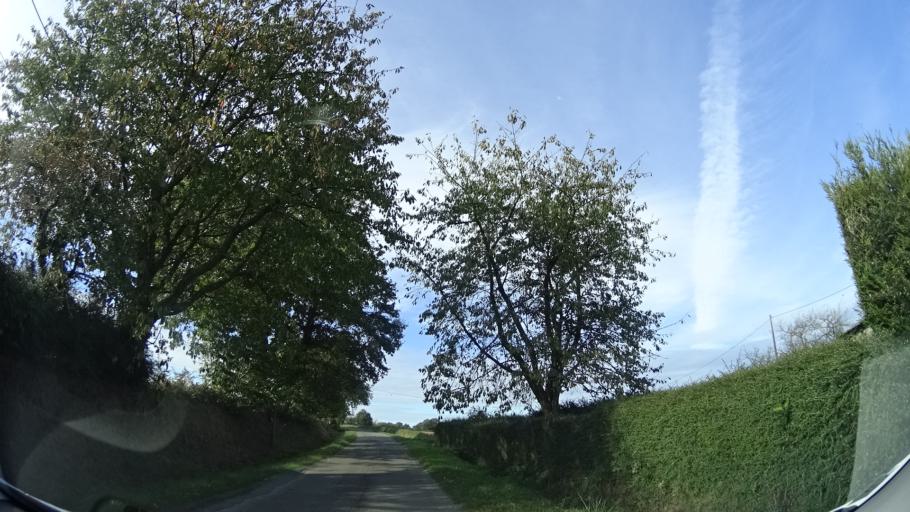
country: FR
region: Brittany
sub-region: Departement d'Ille-et-Vilaine
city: Geveze
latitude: 48.2364
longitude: -1.8164
